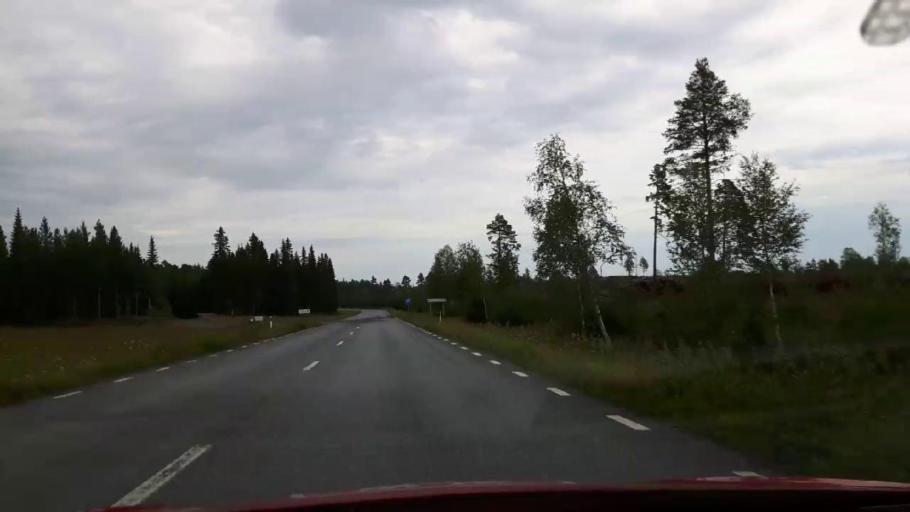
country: SE
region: Jaemtland
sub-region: Stroemsunds Kommun
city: Stroemsund
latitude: 63.5396
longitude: 15.3611
